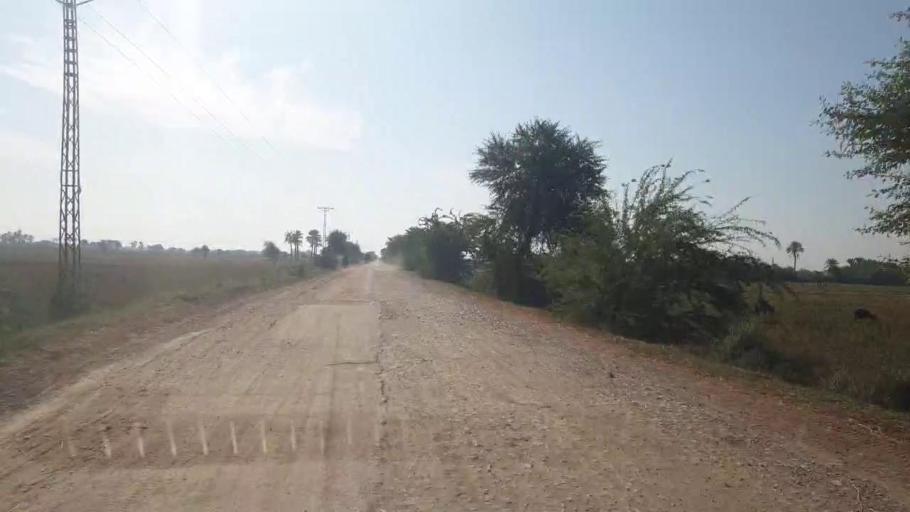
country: PK
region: Sindh
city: Talhar
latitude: 24.9080
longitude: 68.8204
